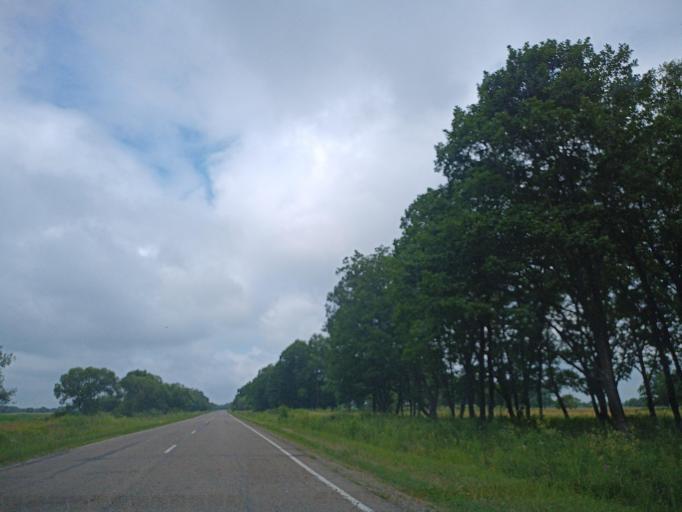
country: RU
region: Primorskiy
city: Dal'nerechensk
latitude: 45.9476
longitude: 133.8991
